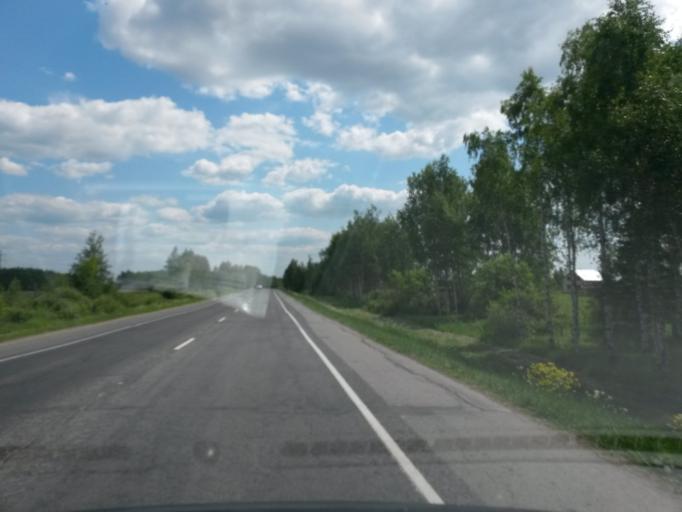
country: RU
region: Jaroslavl
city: Yaroslavl
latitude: 57.5566
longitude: 39.8677
